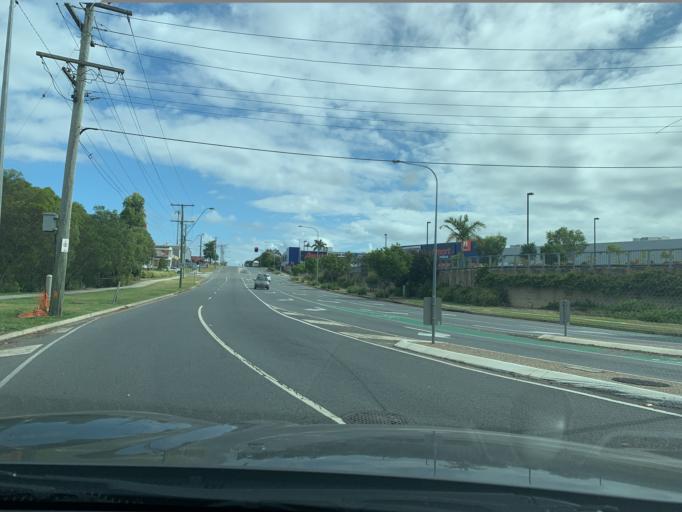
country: AU
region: Queensland
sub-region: Brisbane
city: Wynnum West
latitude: -27.4759
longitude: 153.1408
